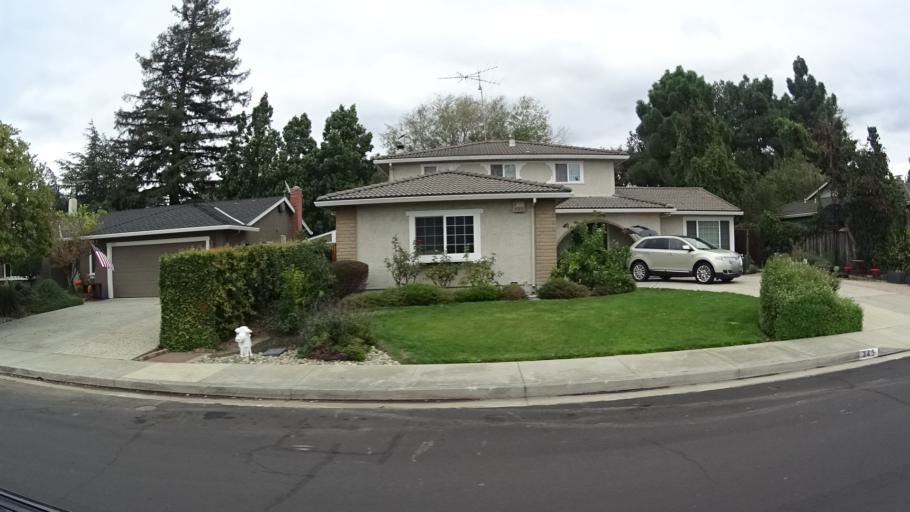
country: US
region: California
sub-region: Santa Clara County
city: Santa Clara
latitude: 37.3291
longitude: -121.9683
